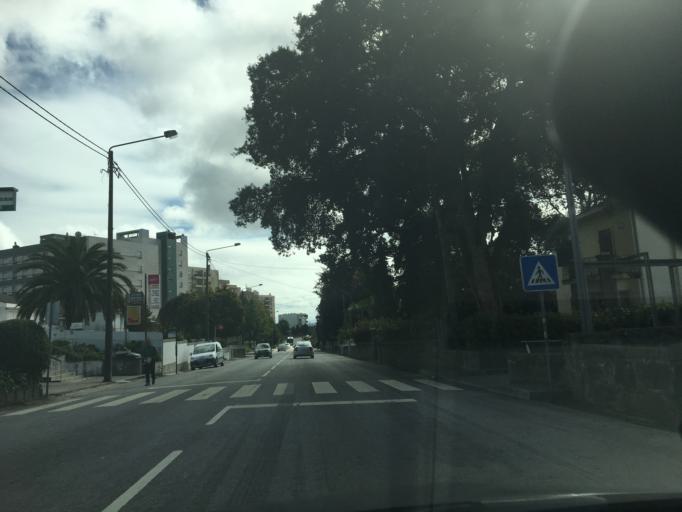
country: PT
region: Porto
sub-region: Maia
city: Gemunde
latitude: 41.2522
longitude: -8.6519
